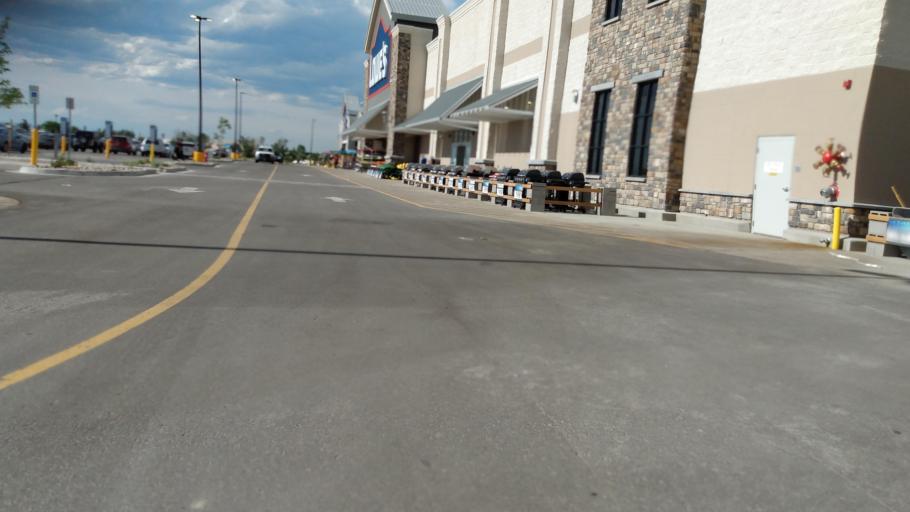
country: US
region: Colorado
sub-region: Boulder County
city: Lafayette
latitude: 40.0133
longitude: -105.1006
